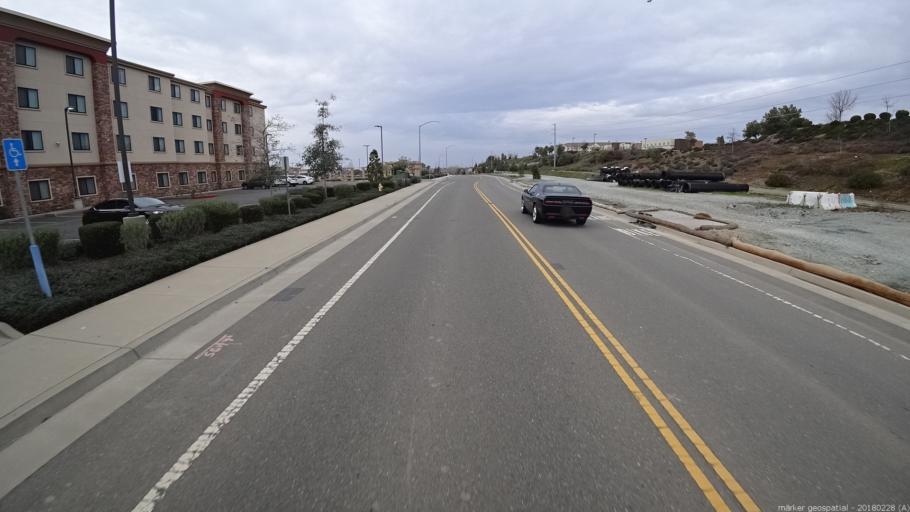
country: US
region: California
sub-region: El Dorado County
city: El Dorado Hills
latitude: 38.6448
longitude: -121.1116
